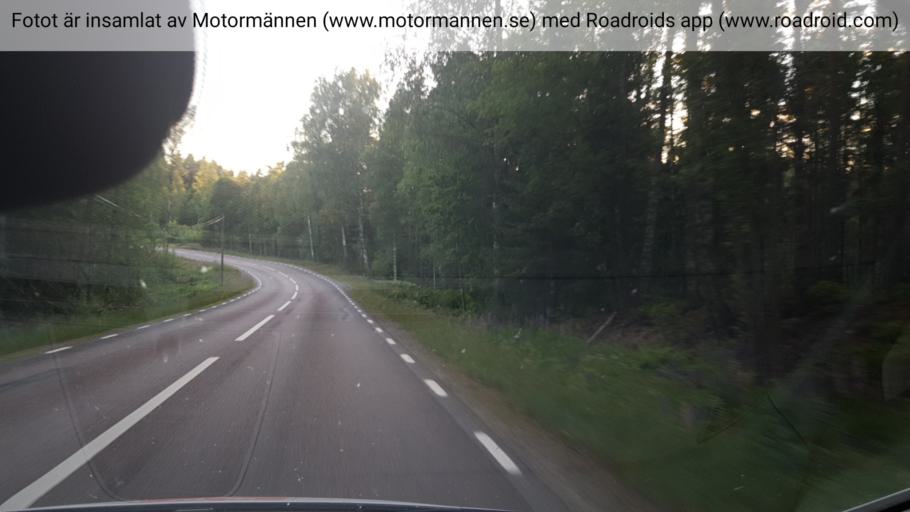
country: SE
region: Vaermland
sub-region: Sunne Kommun
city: Sunne
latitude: 59.6679
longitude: 12.9721
